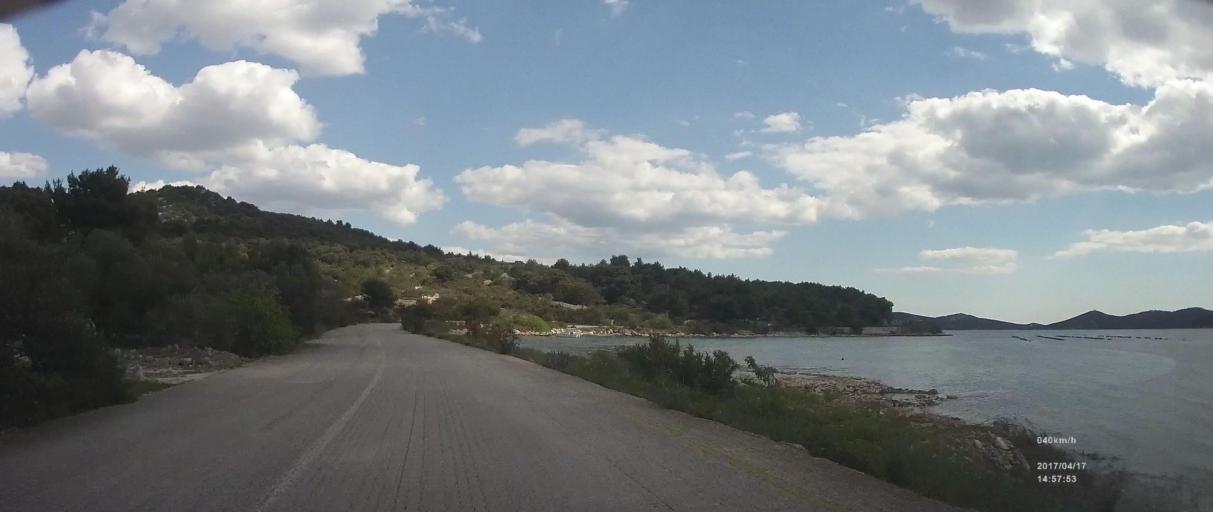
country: HR
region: Sibensko-Kniniska
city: Murter
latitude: 43.8414
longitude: 15.6265
